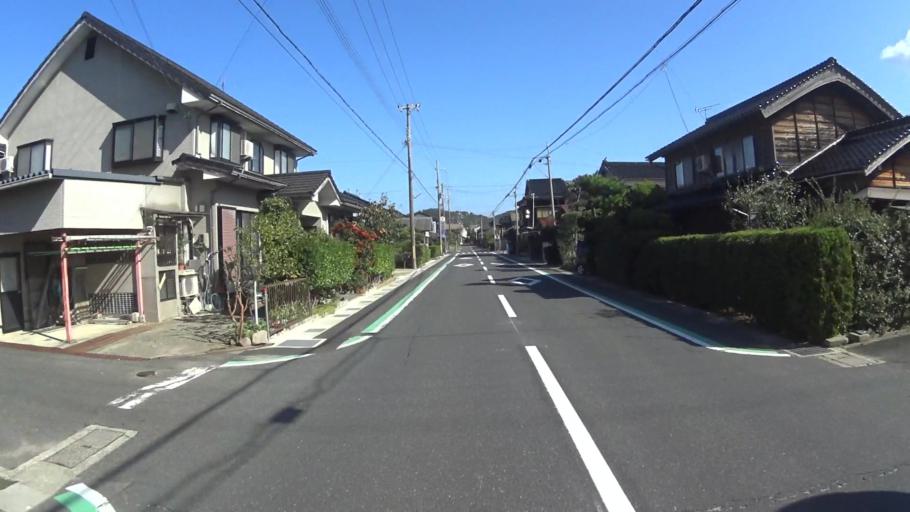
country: JP
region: Kyoto
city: Miyazu
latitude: 35.6877
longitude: 135.0336
